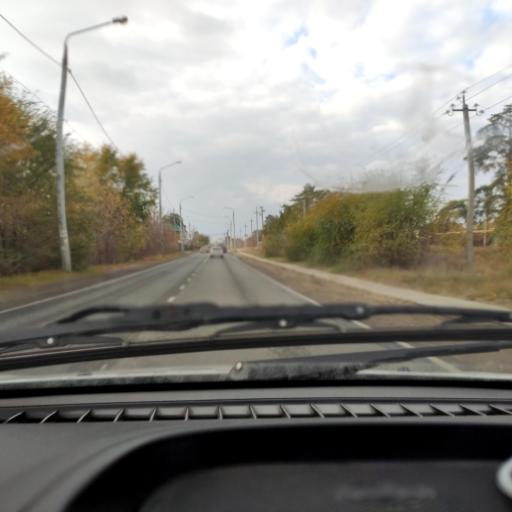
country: RU
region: Samara
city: Zhigulevsk
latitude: 53.4657
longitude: 49.6077
